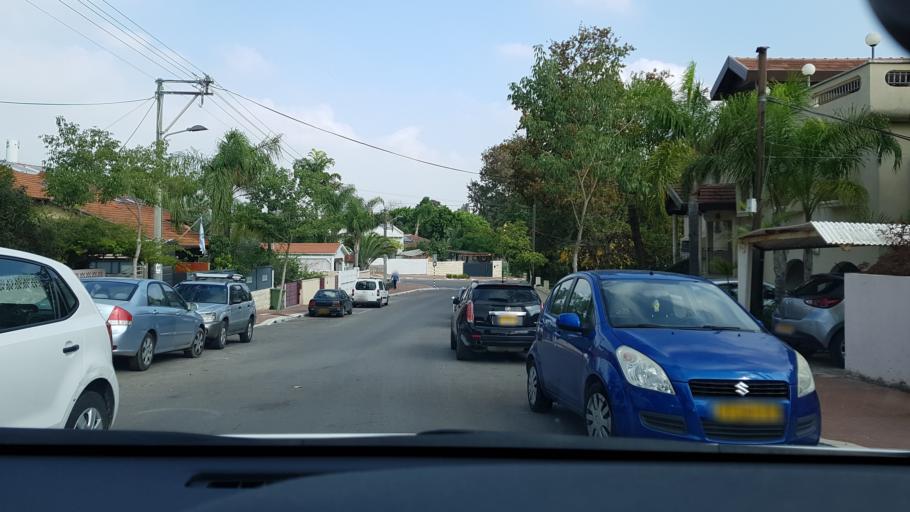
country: IL
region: Central District
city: Mazkeret Batya
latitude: 31.8748
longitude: 34.8178
